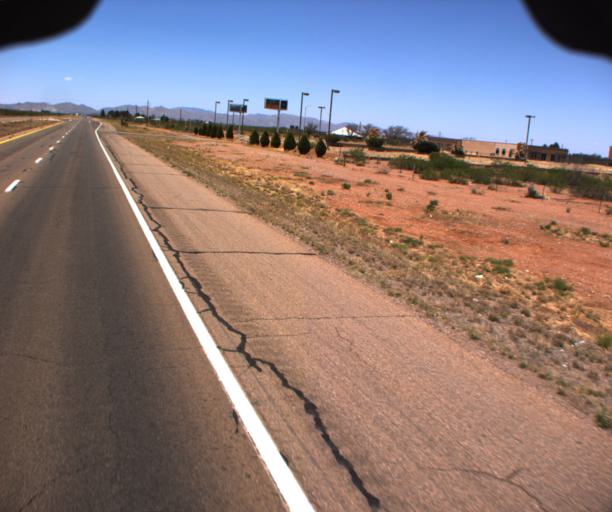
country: US
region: Arizona
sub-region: Cochise County
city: Pirtleville
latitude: 31.3551
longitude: -109.6105
